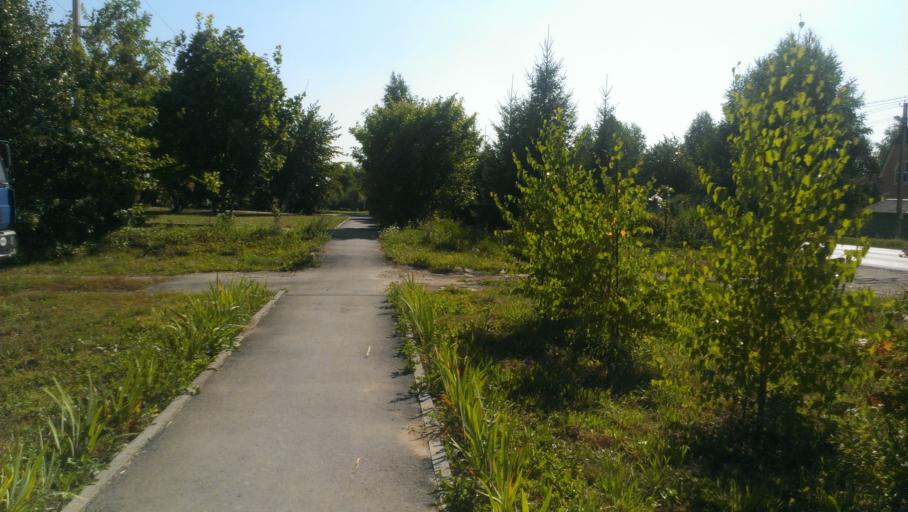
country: RU
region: Altai Krai
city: Novosilikatnyy
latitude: 53.3615
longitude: 83.6423
